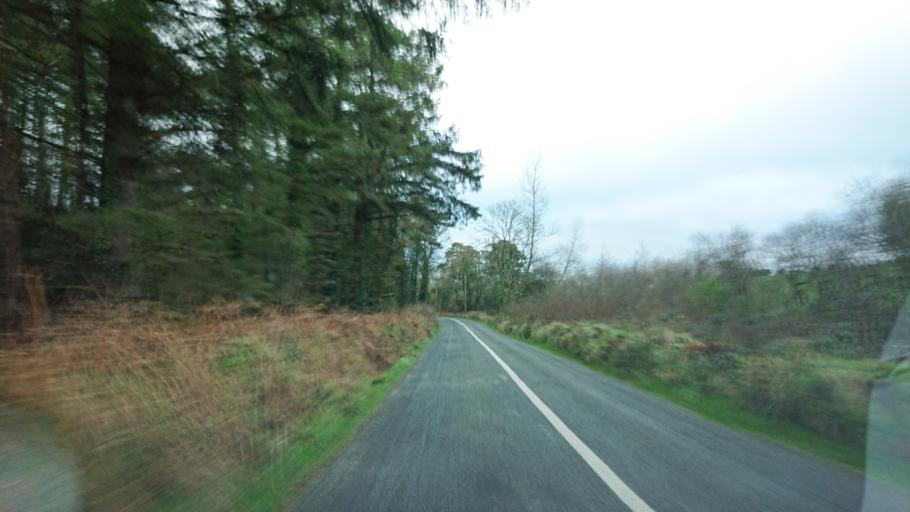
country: IE
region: Munster
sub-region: Waterford
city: Portlaw
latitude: 52.2381
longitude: -7.4140
